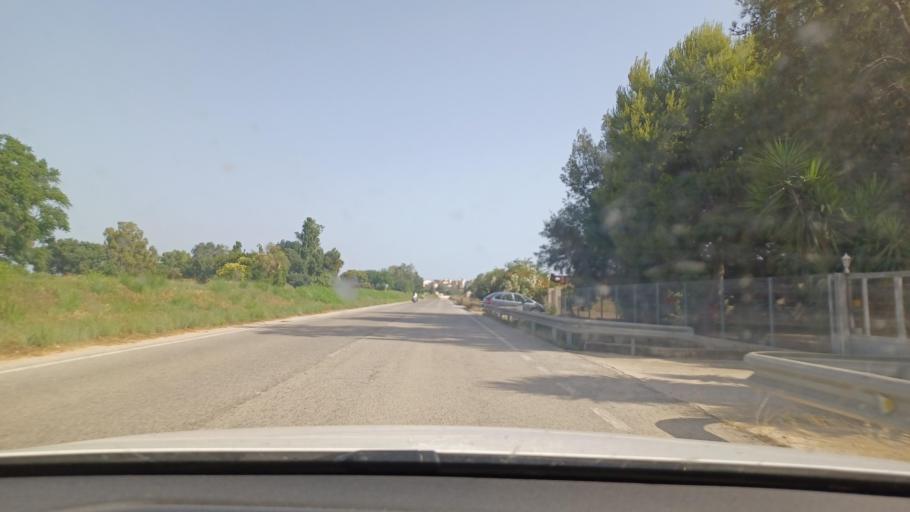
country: ES
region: Catalonia
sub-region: Provincia de Tarragona
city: Amposta
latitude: 40.7234
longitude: 0.5730
